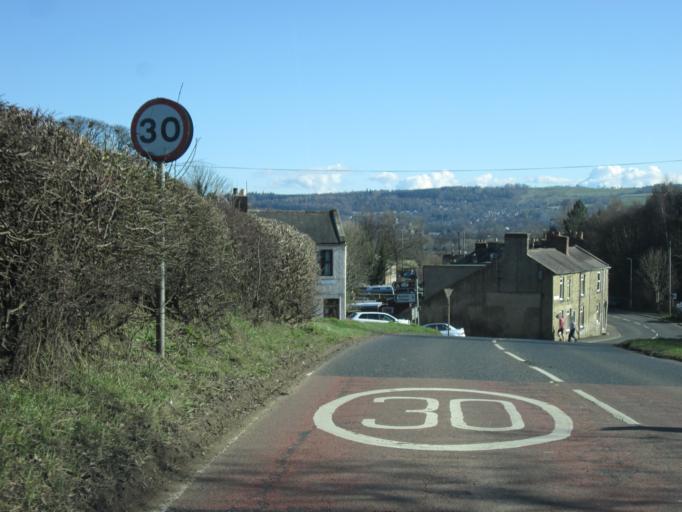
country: GB
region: England
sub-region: Northumberland
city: Acomb
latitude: 54.9921
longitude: -2.1166
